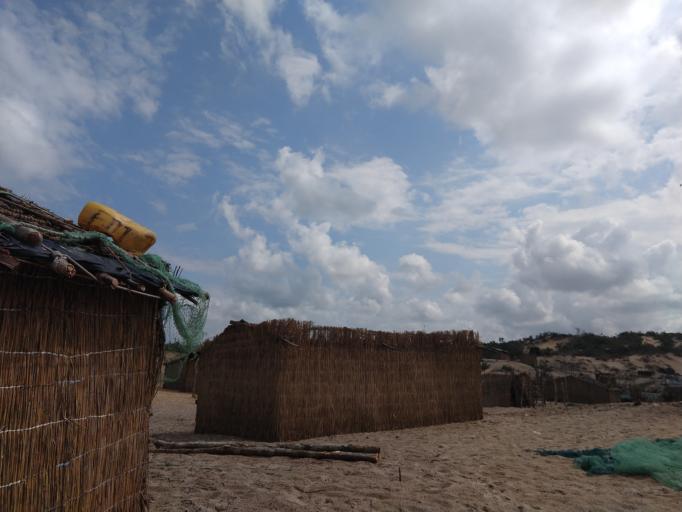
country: MZ
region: Sofala
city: Beira
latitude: -19.6486
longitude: 35.1796
